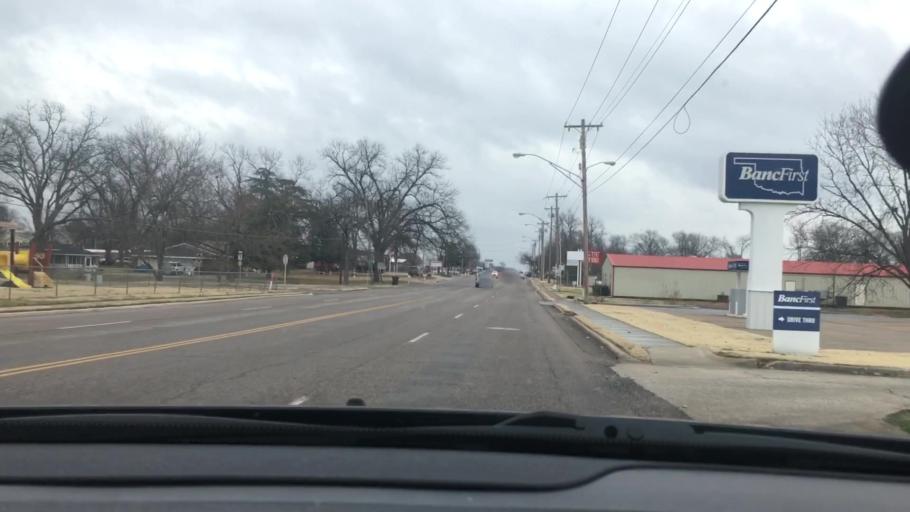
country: US
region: Oklahoma
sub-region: Johnston County
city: Tishomingo
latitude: 34.2306
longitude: -96.6690
